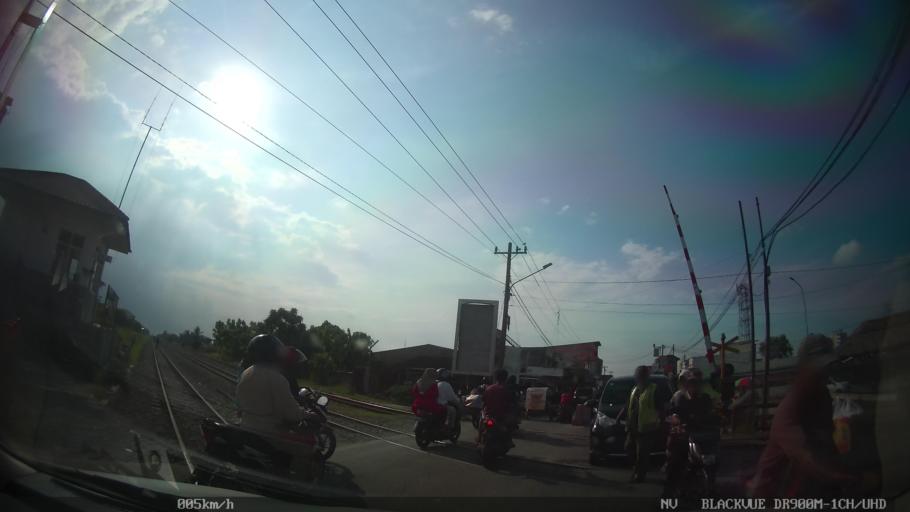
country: ID
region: North Sumatra
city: Medan
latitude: 3.5937
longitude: 98.7548
